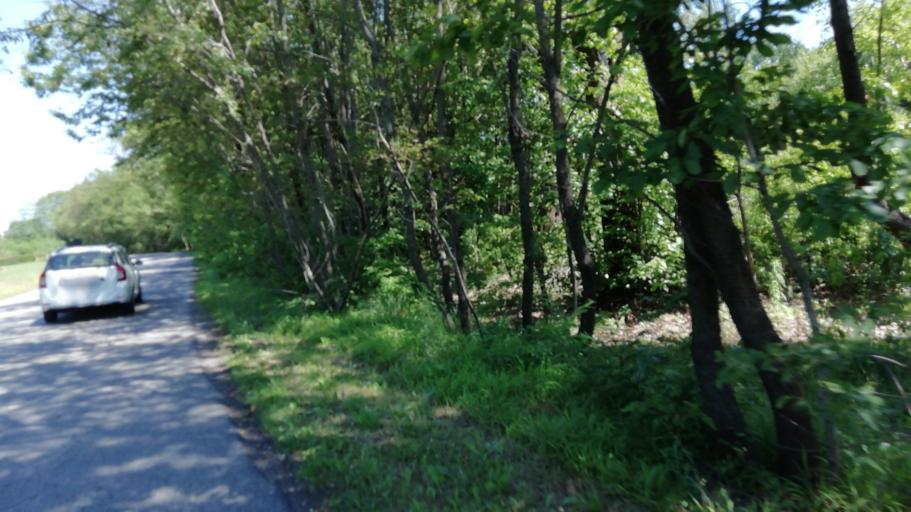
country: IT
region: Lombardy
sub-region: Provincia di Varese
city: Ferno
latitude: 45.6279
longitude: 8.7483
